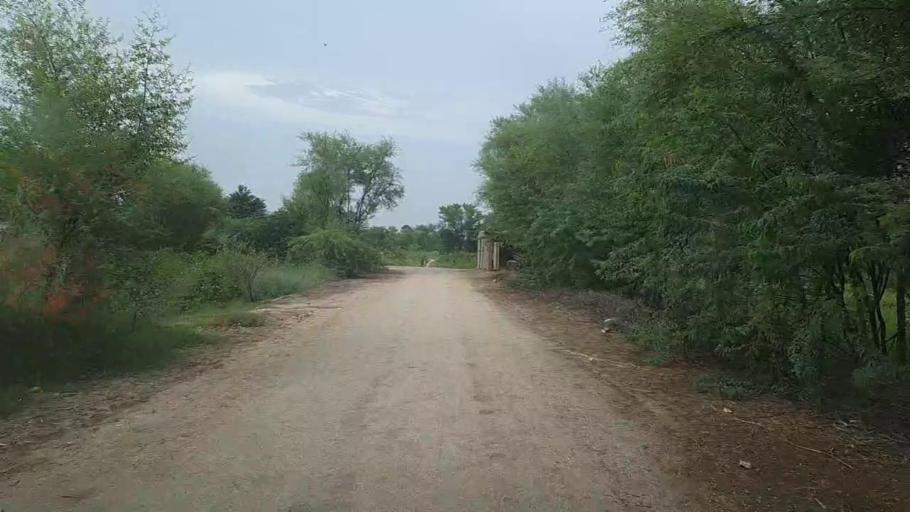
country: PK
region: Sindh
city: Karaundi
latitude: 26.9587
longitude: 68.4147
